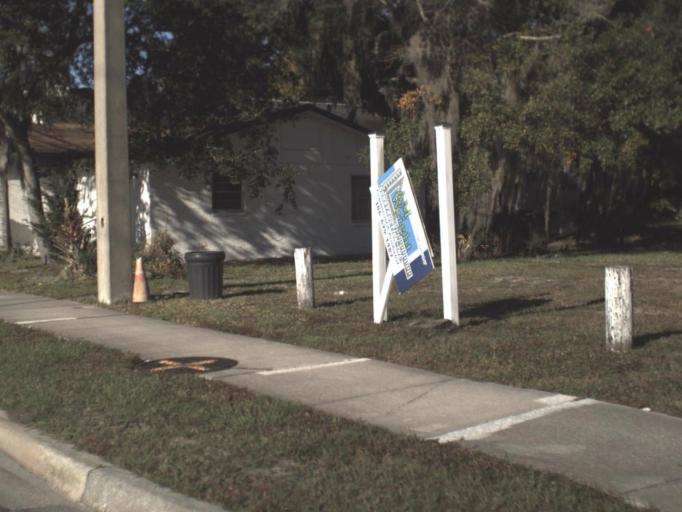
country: US
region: Florida
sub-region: Volusia County
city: Daytona Beach
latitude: 29.2127
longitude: -81.0401
